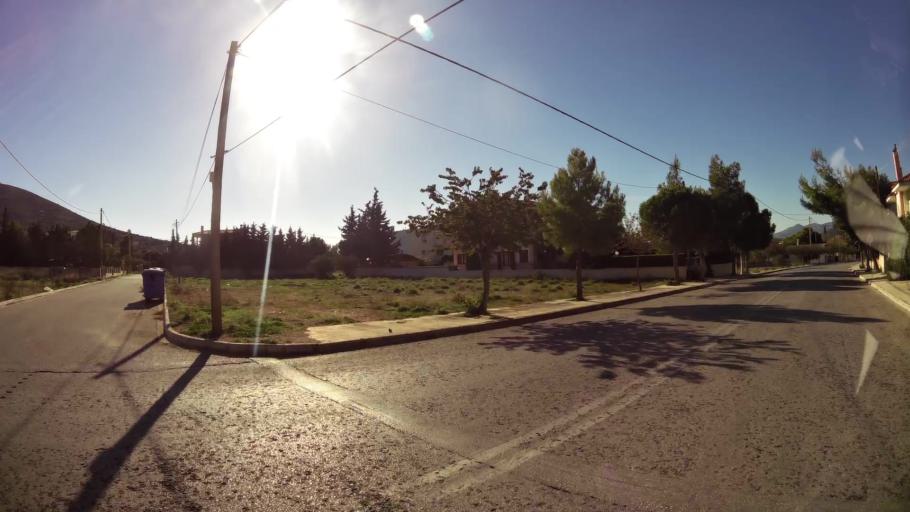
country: GR
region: Attica
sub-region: Nomarchia Anatolikis Attikis
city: Kalyvia Thorikou
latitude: 37.8347
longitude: 23.9260
